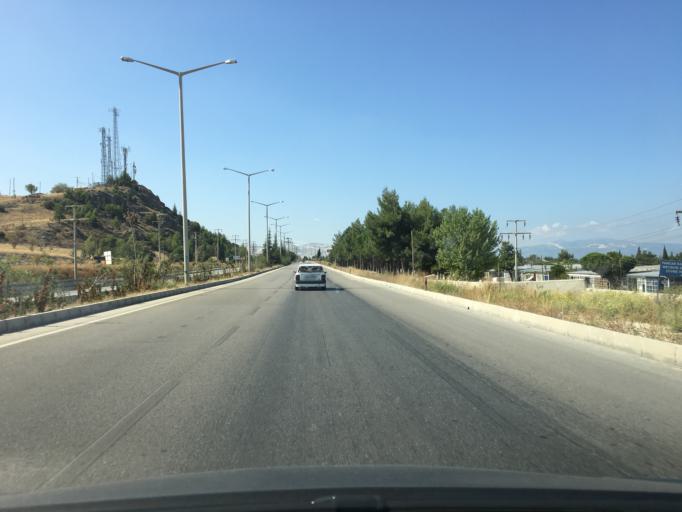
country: TR
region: Burdur
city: Burdur
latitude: 37.7462
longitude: 30.3189
